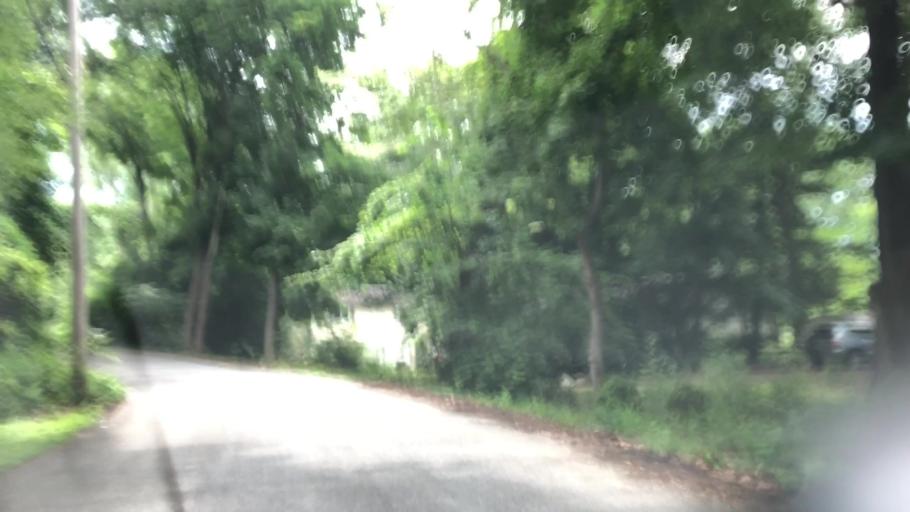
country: US
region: Ohio
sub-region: Summit County
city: Portage Lakes
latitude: 41.0100
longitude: -81.5344
